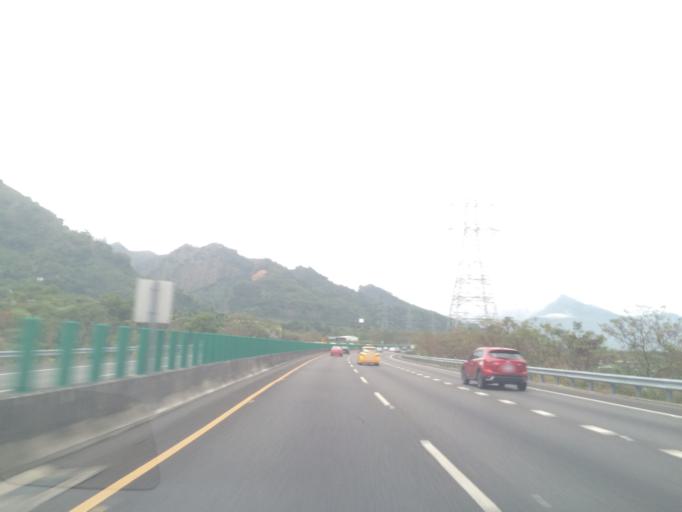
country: TW
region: Taiwan
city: Zhongxing New Village
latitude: 23.9937
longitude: 120.8011
